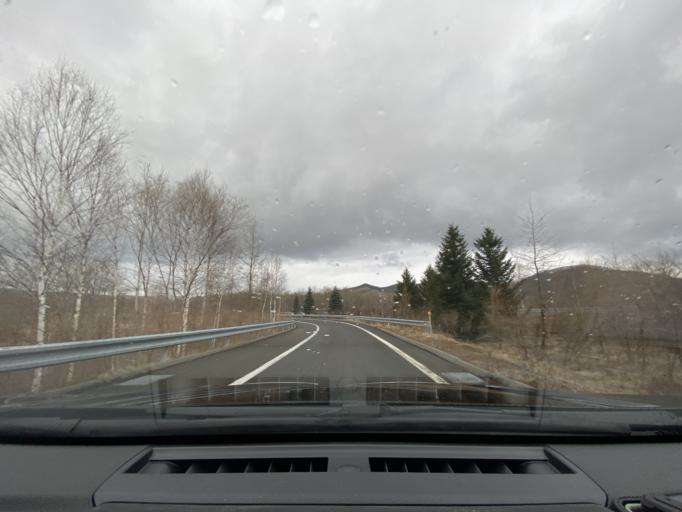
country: JP
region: Hokkaido
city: Otofuke
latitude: 43.2094
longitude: 143.5612
